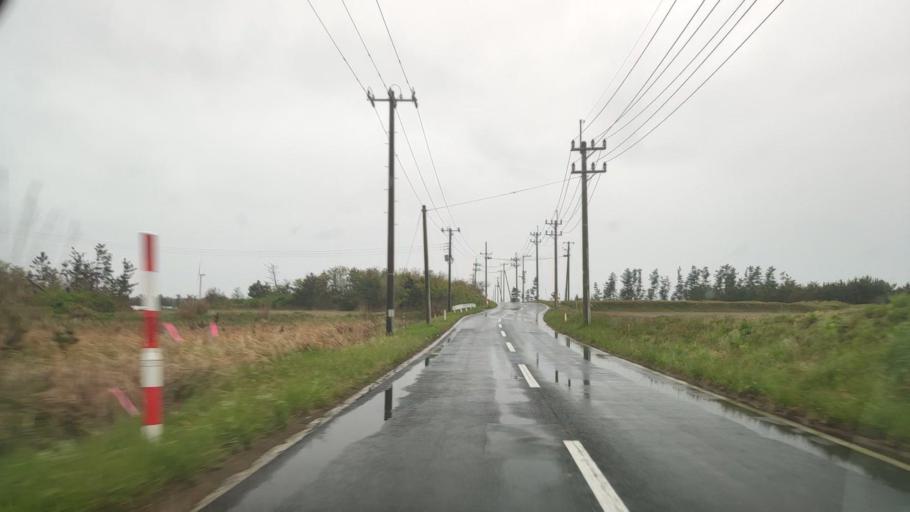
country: JP
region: Akita
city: Noshiromachi
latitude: 40.0953
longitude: 139.9740
